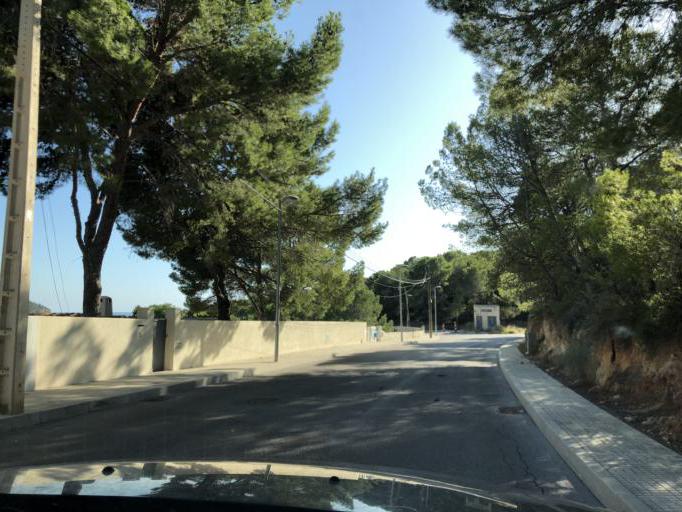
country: ES
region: Balearic Islands
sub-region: Illes Balears
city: Camp de Mar
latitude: 39.5421
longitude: 2.4073
